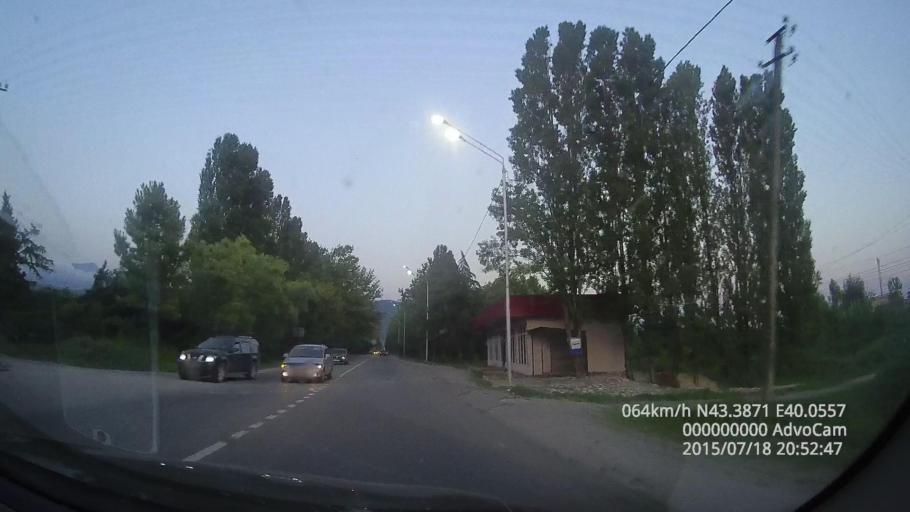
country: GE
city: Gantiadi
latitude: 43.3869
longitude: 40.0571
